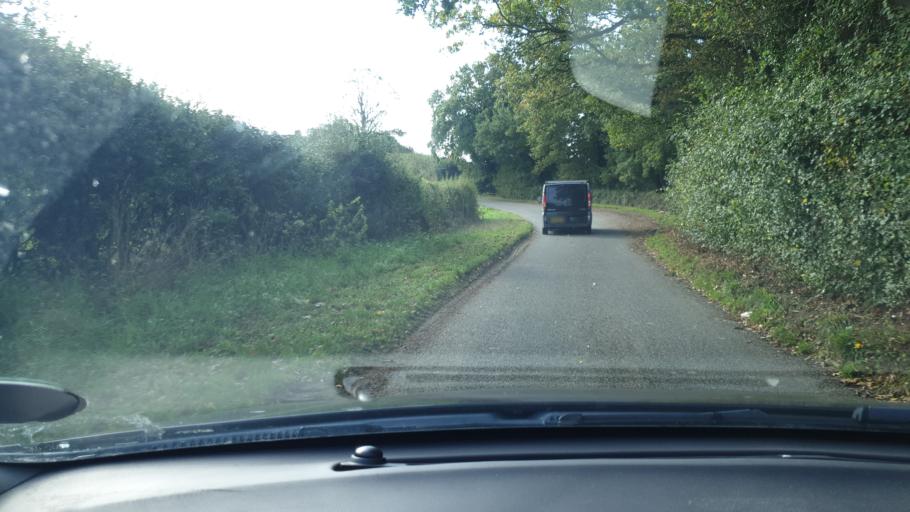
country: GB
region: England
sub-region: Essex
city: Alresford
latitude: 51.8640
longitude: 1.0180
